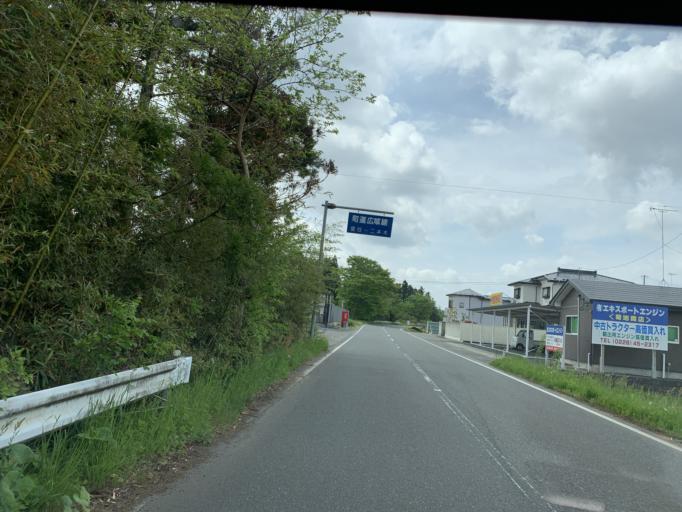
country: JP
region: Iwate
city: Ichinoseki
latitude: 38.8267
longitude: 141.0212
